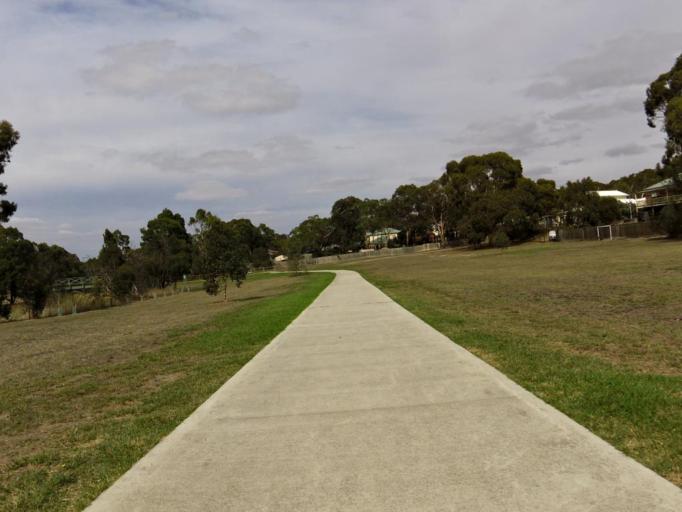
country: AU
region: Victoria
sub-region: Hume
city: Sunbury
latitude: -37.5656
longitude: 144.7024
